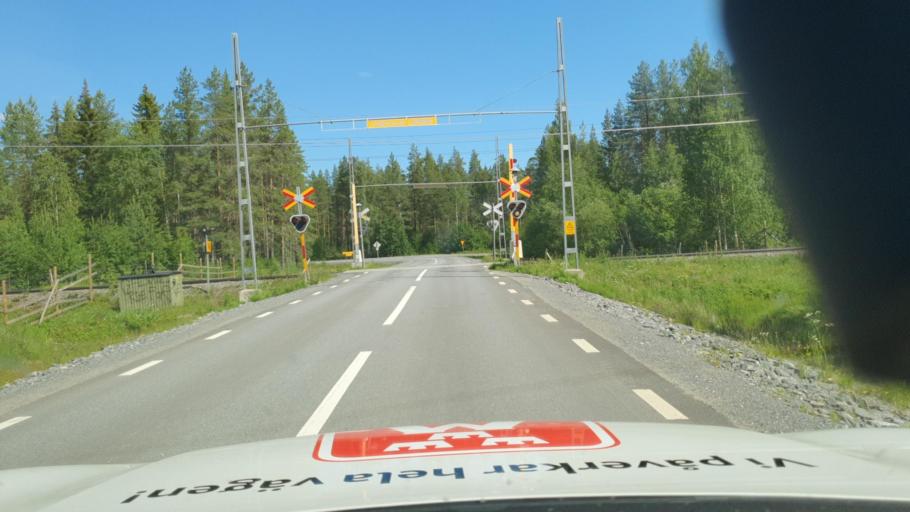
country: SE
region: Vaesterbotten
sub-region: Skelleftea Kommun
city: Langsele
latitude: 64.7753
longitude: 20.3377
